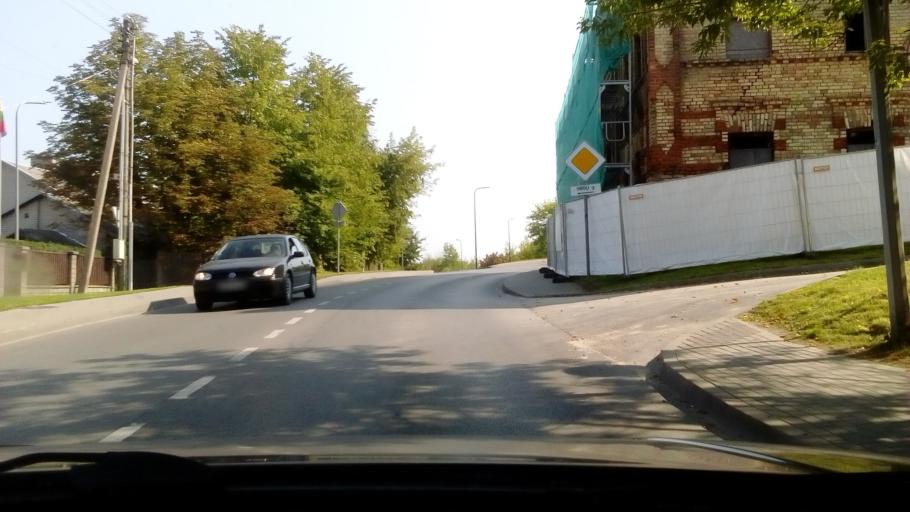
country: LT
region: Alytaus apskritis
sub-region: Alytus
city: Alytus
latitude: 54.4012
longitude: 24.0476
